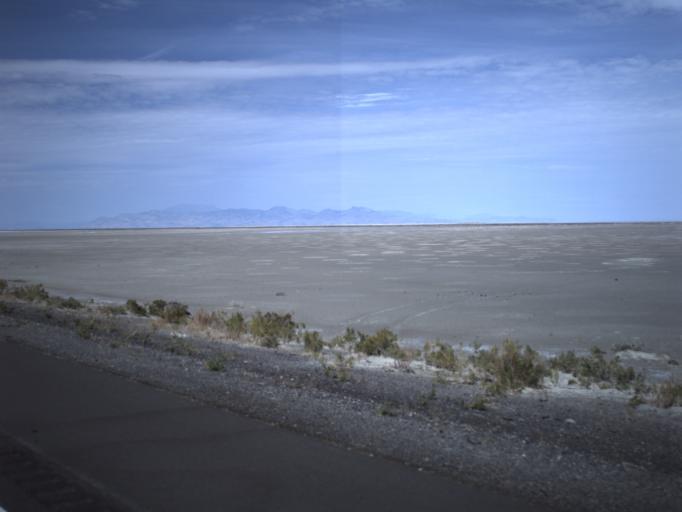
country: US
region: Utah
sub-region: Tooele County
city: Wendover
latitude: 40.7287
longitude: -113.3547
